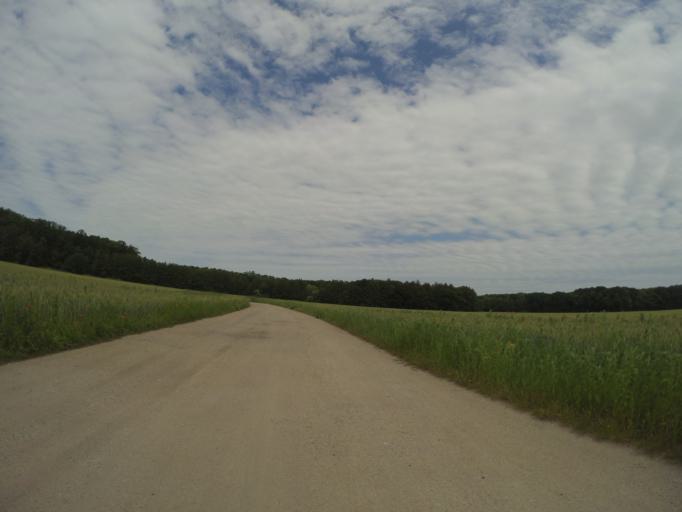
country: CZ
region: Central Bohemia
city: Celakovice
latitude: 50.1748
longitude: 14.7842
